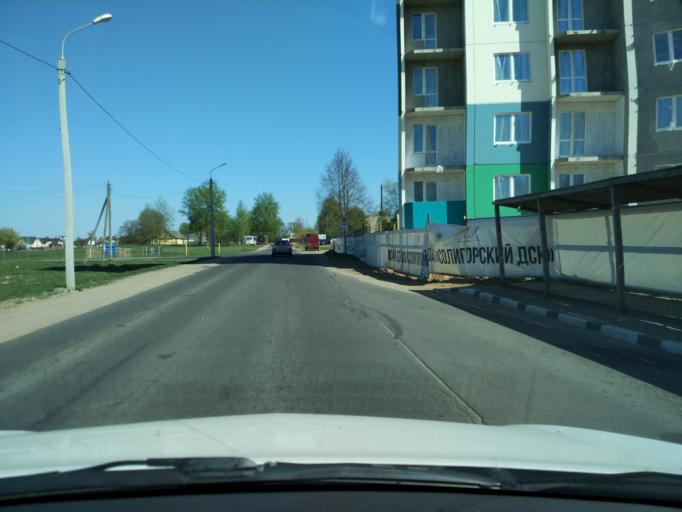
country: BY
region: Minsk
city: Lyeskawka
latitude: 54.0006
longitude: 27.7083
